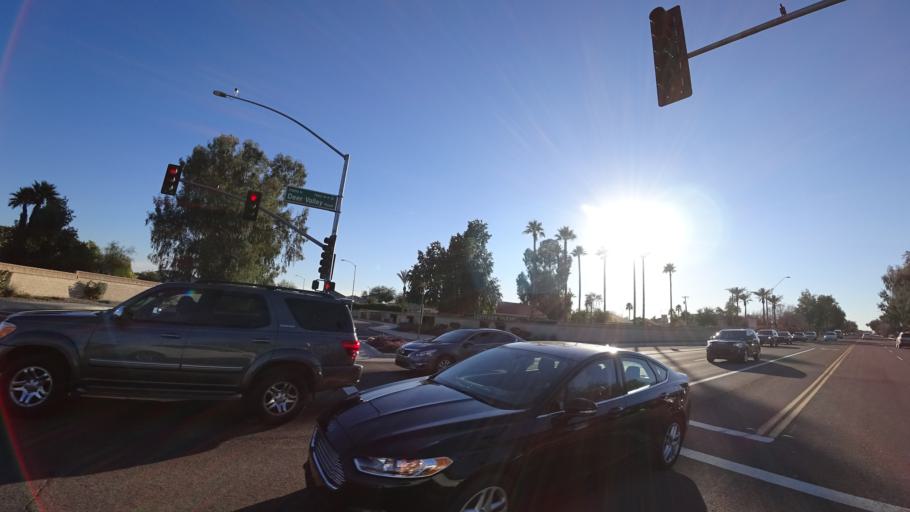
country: US
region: Arizona
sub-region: Maricopa County
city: Sun City
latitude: 33.6817
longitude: -112.2290
